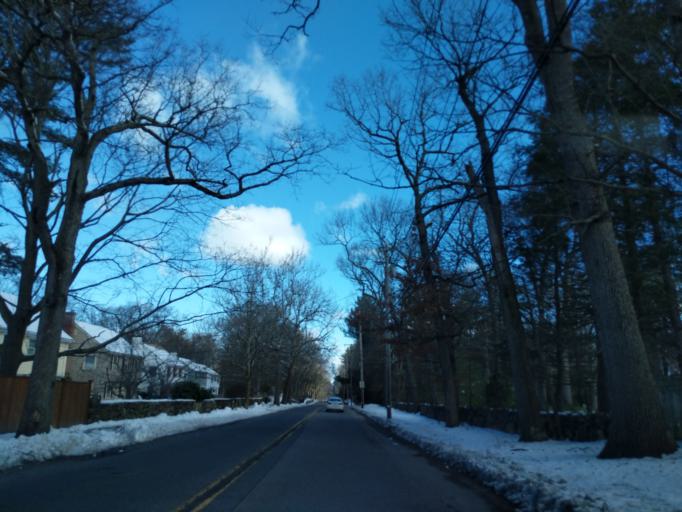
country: US
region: Massachusetts
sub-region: Norfolk County
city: Milton
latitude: 42.2500
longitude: -71.0691
